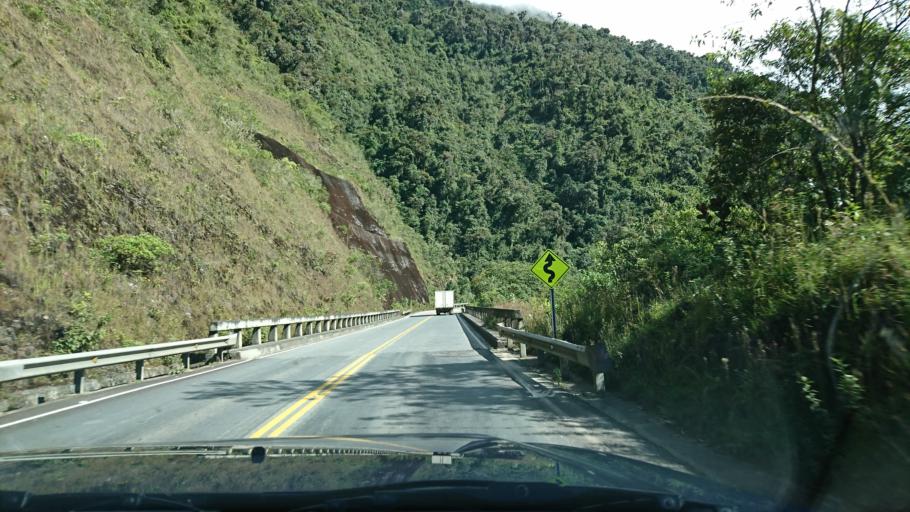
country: BO
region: La Paz
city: Coroico
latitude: -16.2199
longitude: -67.8212
